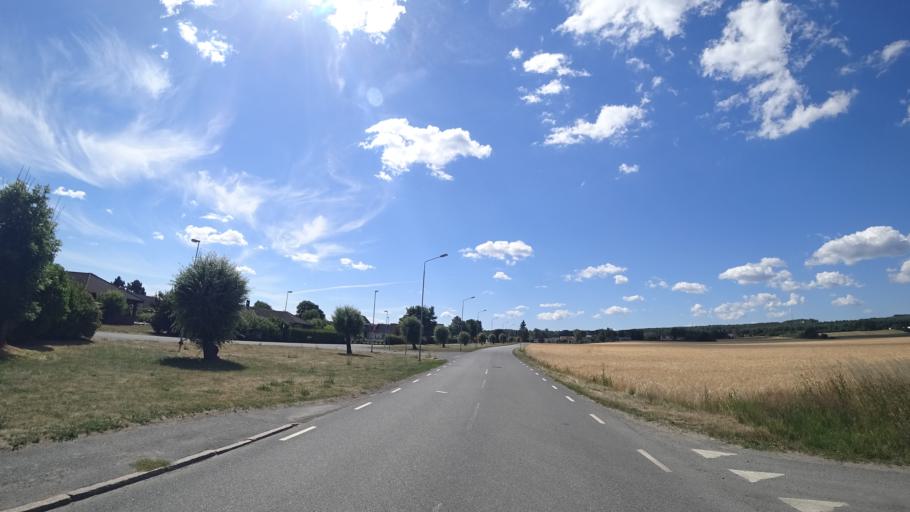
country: SE
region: Skane
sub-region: Kristianstads Kommun
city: Onnestad
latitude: 56.0574
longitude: 14.0187
